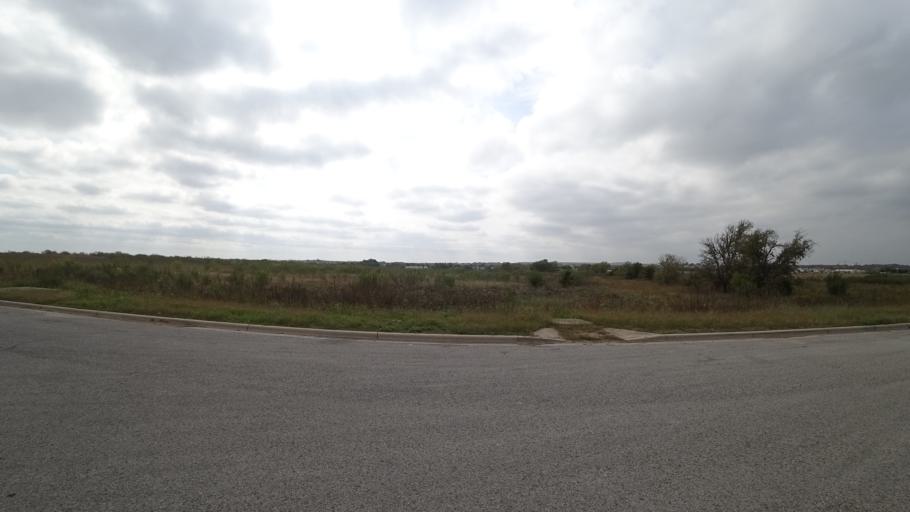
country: US
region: Texas
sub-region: Travis County
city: Manor
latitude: 30.3707
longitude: -97.6079
